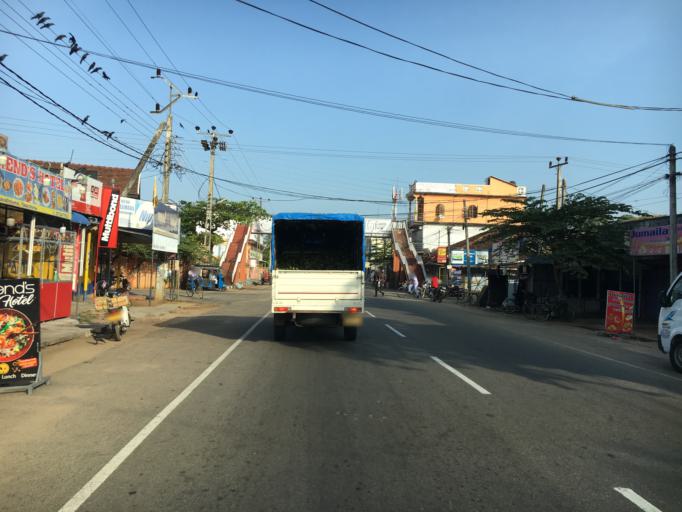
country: LK
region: Eastern Province
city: Eravur Town
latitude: 7.9128
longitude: 81.5259
